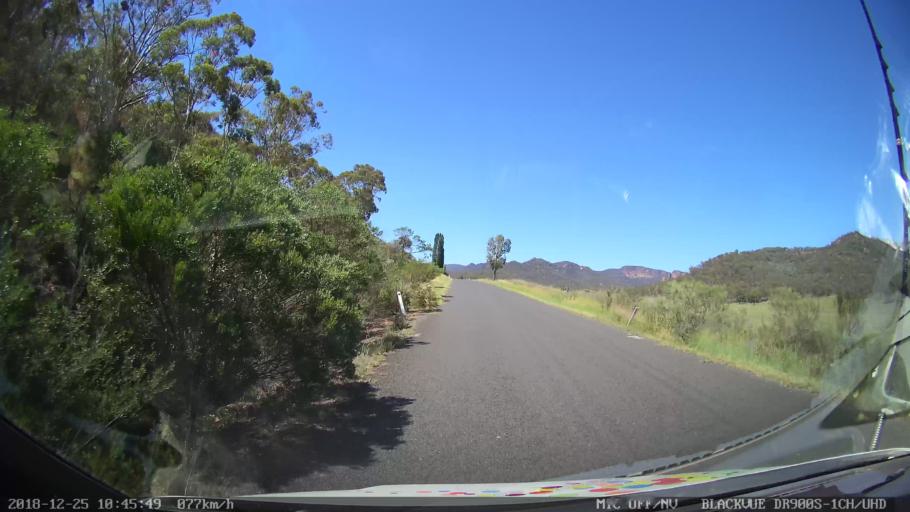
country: AU
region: New South Wales
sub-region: Upper Hunter Shire
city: Merriwa
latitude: -32.4374
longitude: 150.2879
